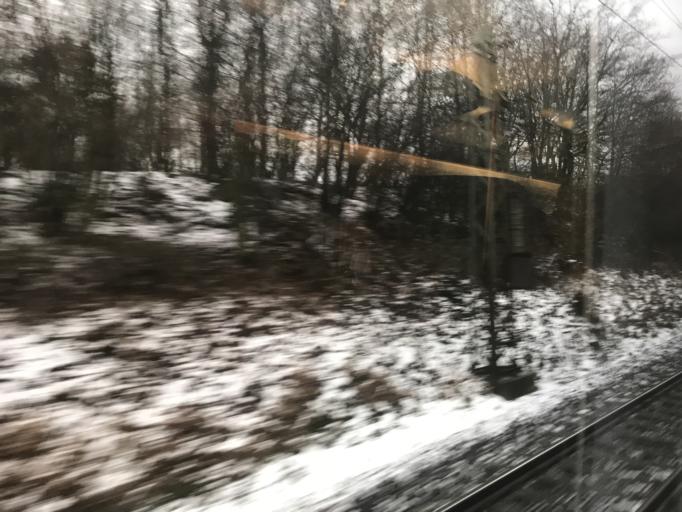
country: DE
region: Hesse
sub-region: Regierungsbezirk Darmstadt
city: Steinau an der Strasse
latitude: 50.3300
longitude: 9.4804
